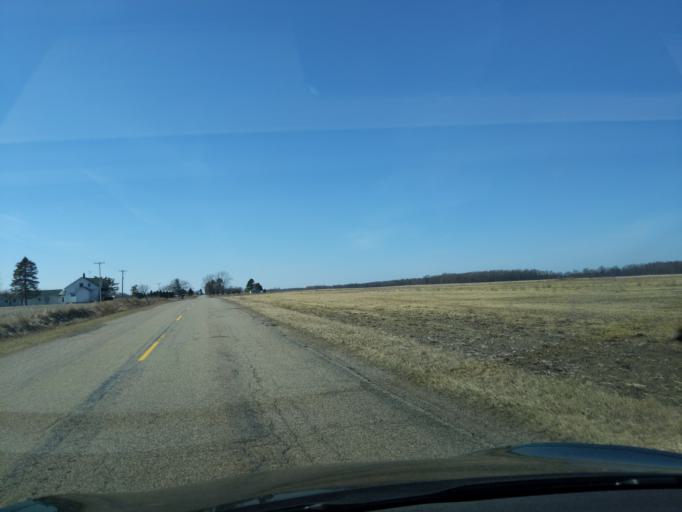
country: US
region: Michigan
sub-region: Ionia County
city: Portland
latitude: 42.7266
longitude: -84.9166
